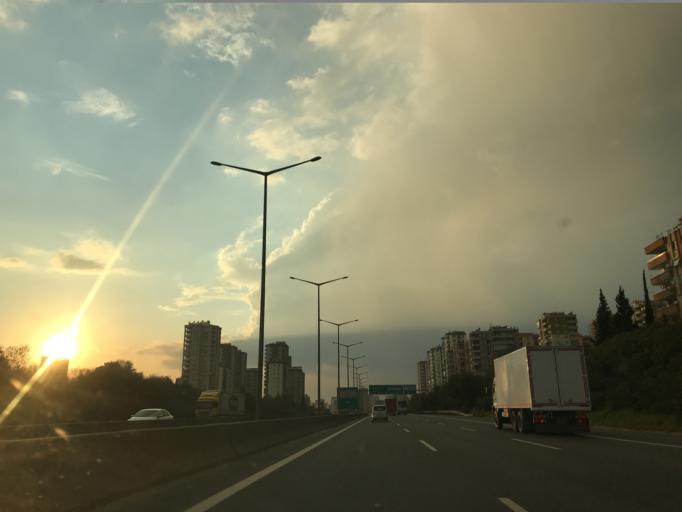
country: TR
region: Adana
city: Seyhan
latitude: 37.0313
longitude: 35.2641
